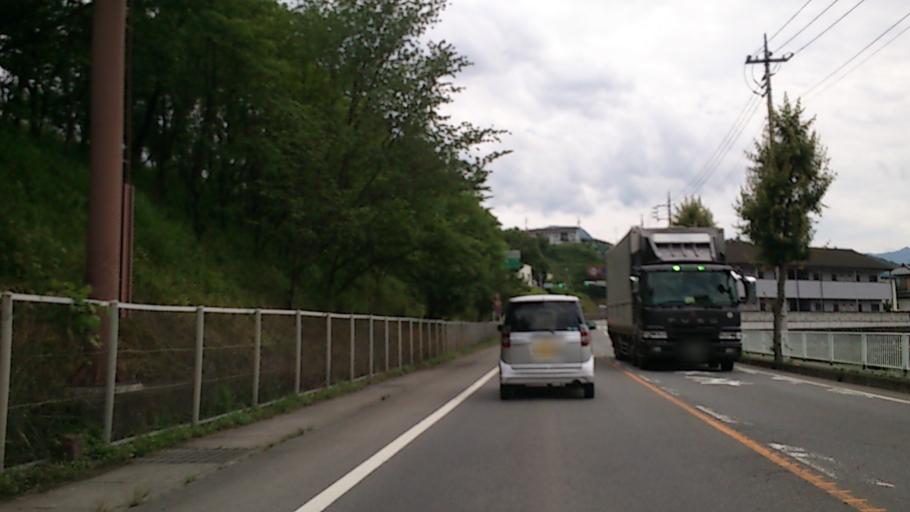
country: JP
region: Gunma
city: Tomioka
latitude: 36.2353
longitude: 138.8225
